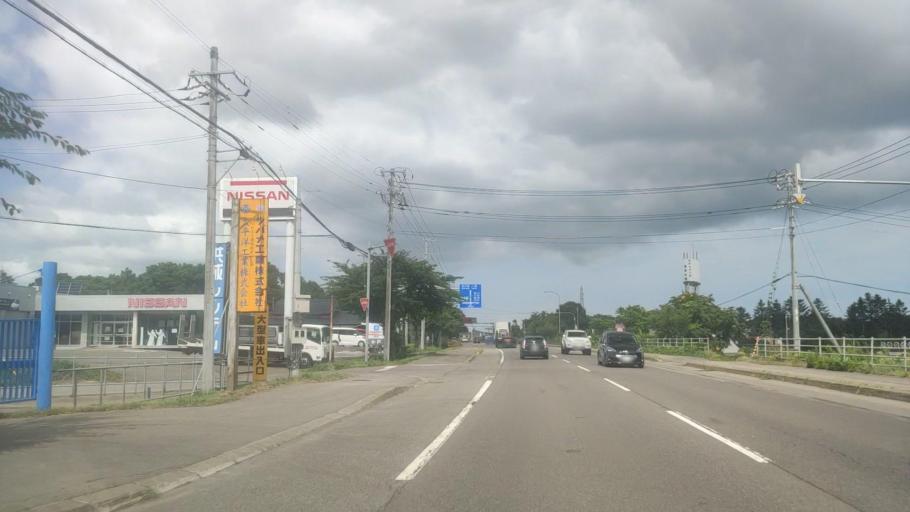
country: JP
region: Hokkaido
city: Nanae
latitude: 42.0895
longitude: 140.5812
